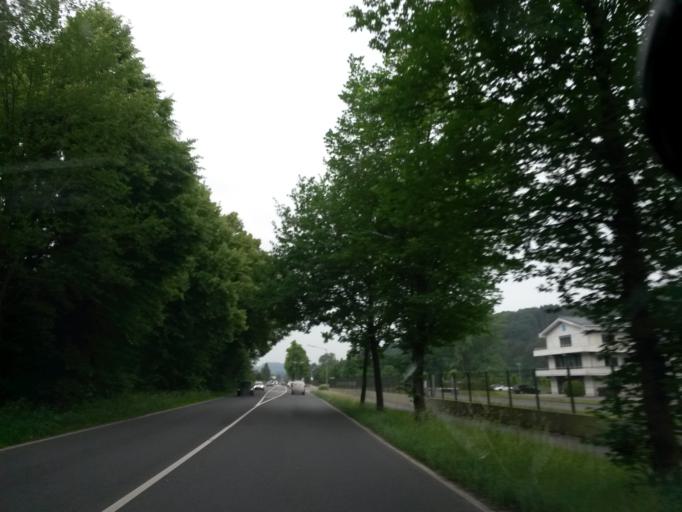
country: DE
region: North Rhine-Westphalia
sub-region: Regierungsbezirk Koln
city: Engelskirchen
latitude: 50.9893
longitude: 7.3945
